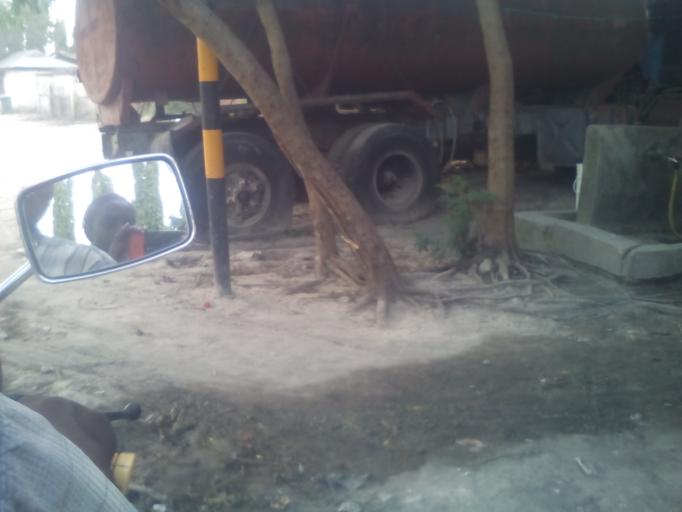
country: TZ
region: Dar es Salaam
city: Dar es Salaam
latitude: -6.8460
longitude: 39.2765
